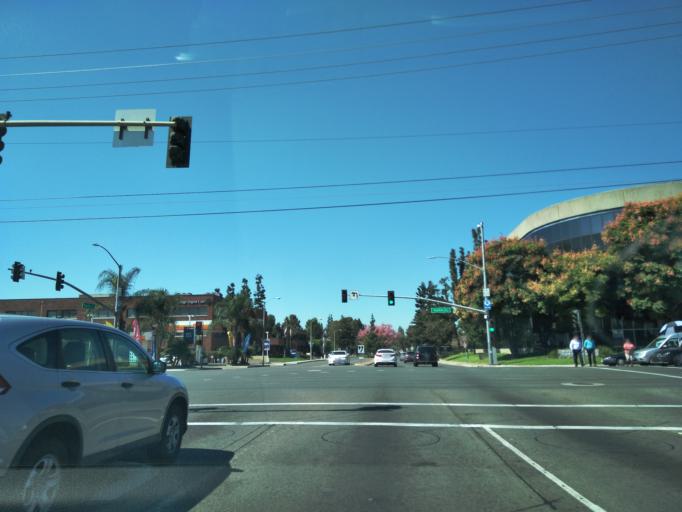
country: US
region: California
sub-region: Orange County
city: Tustin
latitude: 33.7483
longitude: -117.8340
